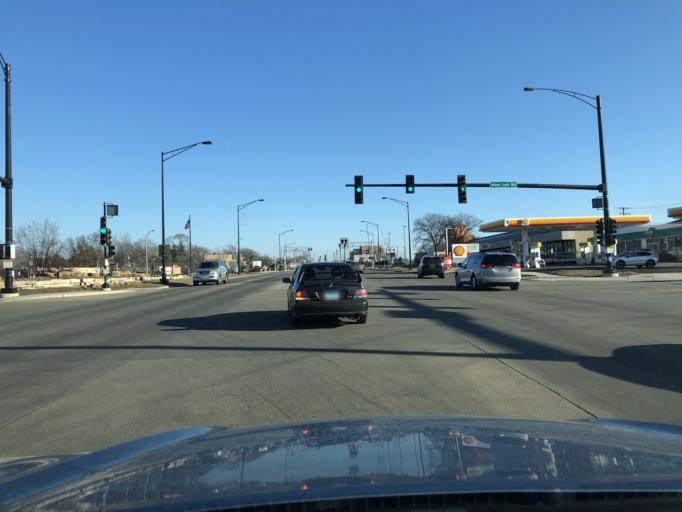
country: US
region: Illinois
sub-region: DuPage County
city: Wood Dale
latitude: 41.9633
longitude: -87.9791
